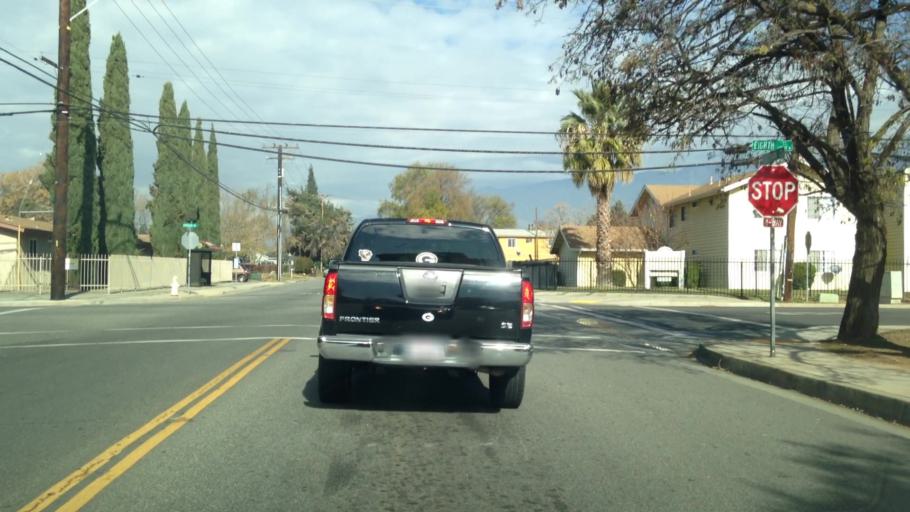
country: US
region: California
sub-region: Riverside County
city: Beaumont
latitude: 33.9322
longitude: -116.9660
